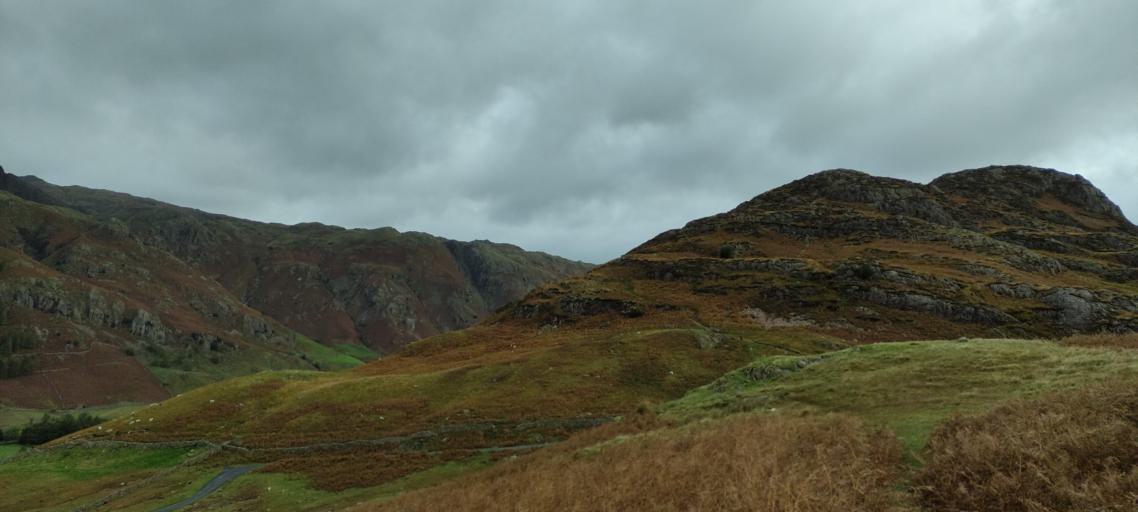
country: GB
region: England
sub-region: Cumbria
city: Ambleside
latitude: 54.4357
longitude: -3.0996
